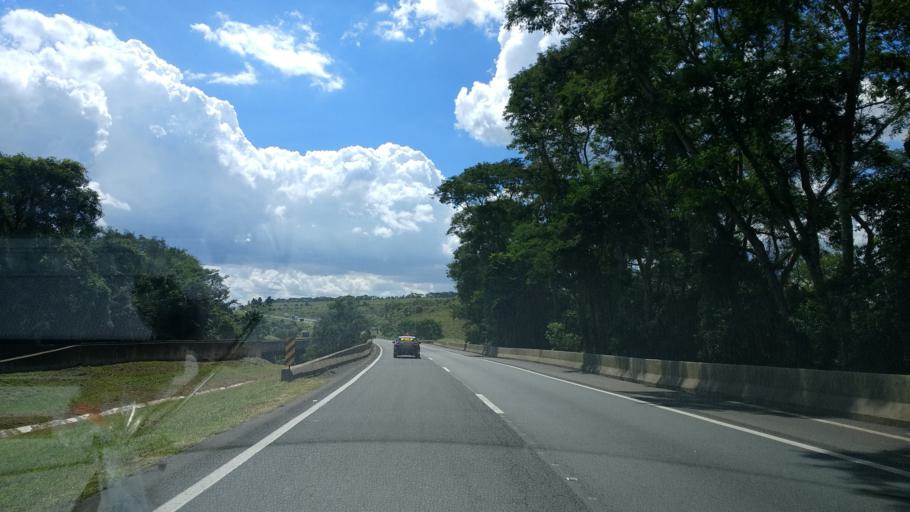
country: BR
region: Parana
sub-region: Palmeira
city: Palmeira
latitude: -25.2450
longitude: -50.0237
